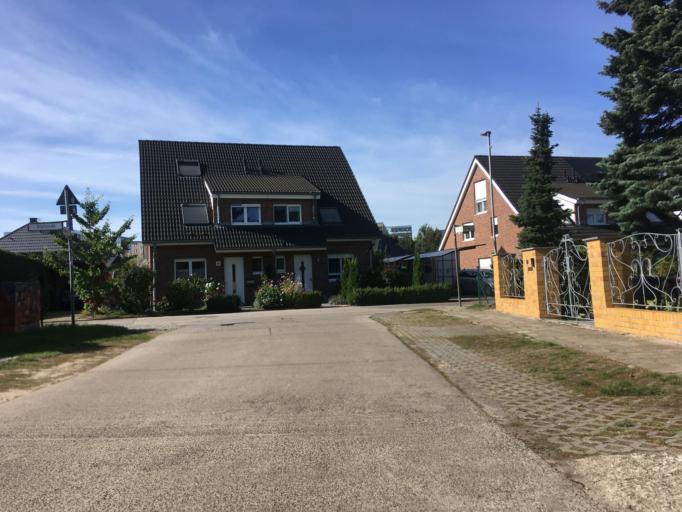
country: DE
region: Berlin
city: Altglienicke
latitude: 52.4024
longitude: 13.5302
